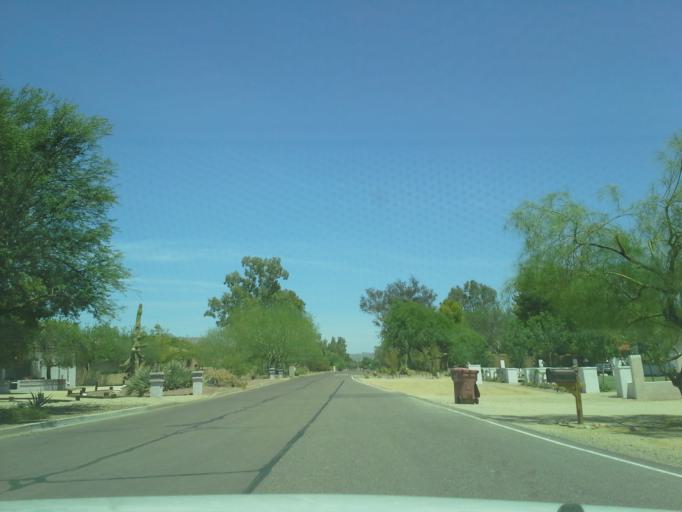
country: US
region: Arizona
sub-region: Maricopa County
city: Scottsdale
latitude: 33.5898
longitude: -111.8711
